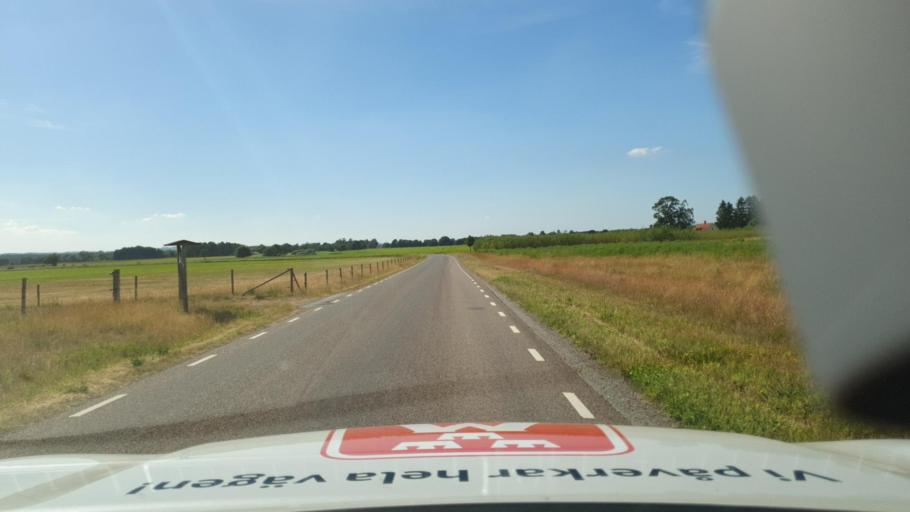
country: SE
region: Skane
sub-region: Sjobo Kommun
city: Sjoebo
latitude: 55.6197
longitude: 13.6478
